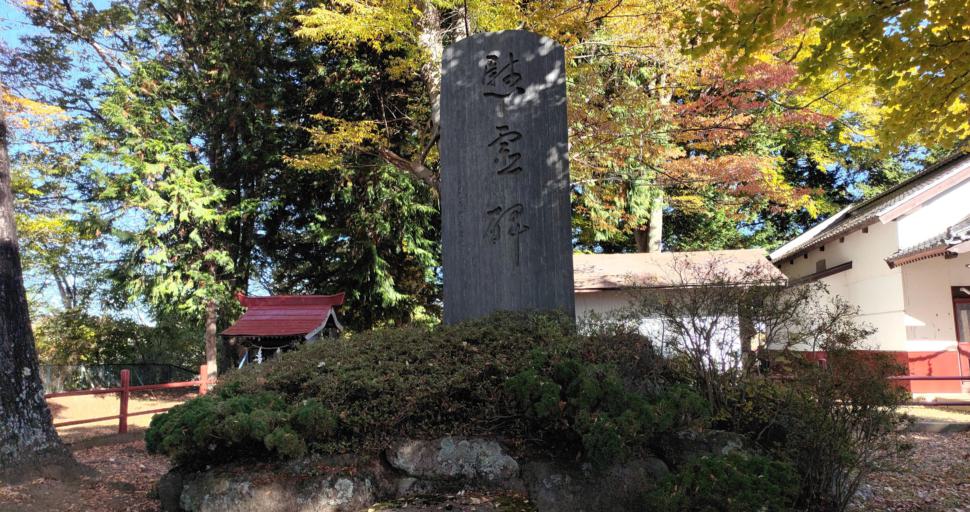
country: JP
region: Nagano
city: Saku
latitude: 36.2440
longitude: 138.4755
